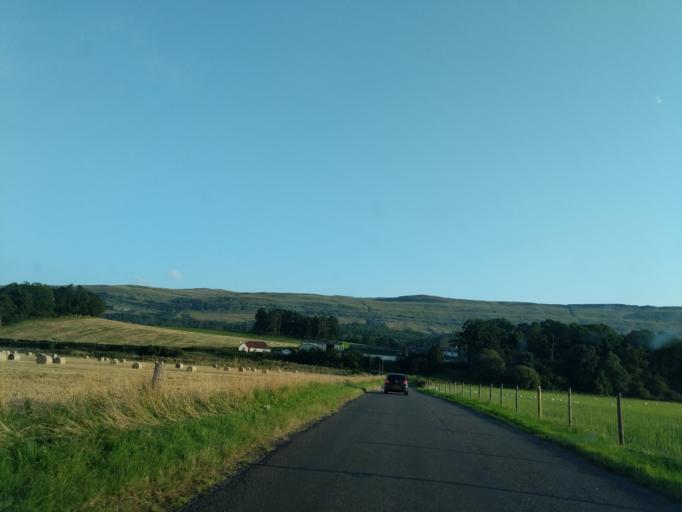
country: GB
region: Scotland
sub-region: Stirling
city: Doune
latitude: 56.1296
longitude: -4.0966
